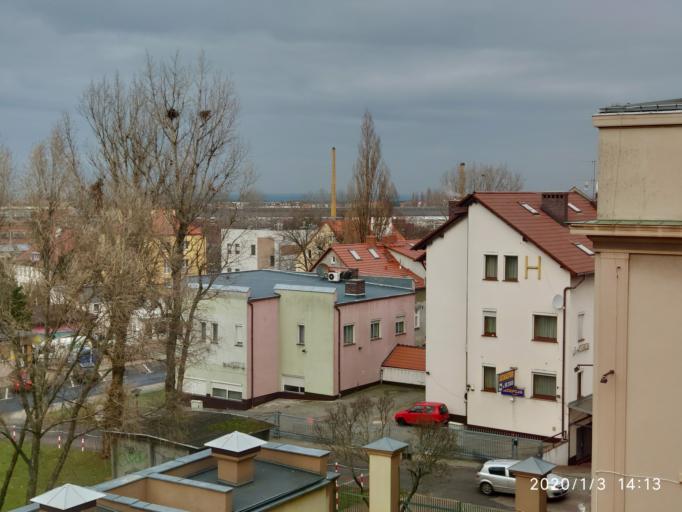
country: PL
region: Lubusz
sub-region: Zielona Gora
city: Zielona Gora
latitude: 51.9440
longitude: 15.5091
